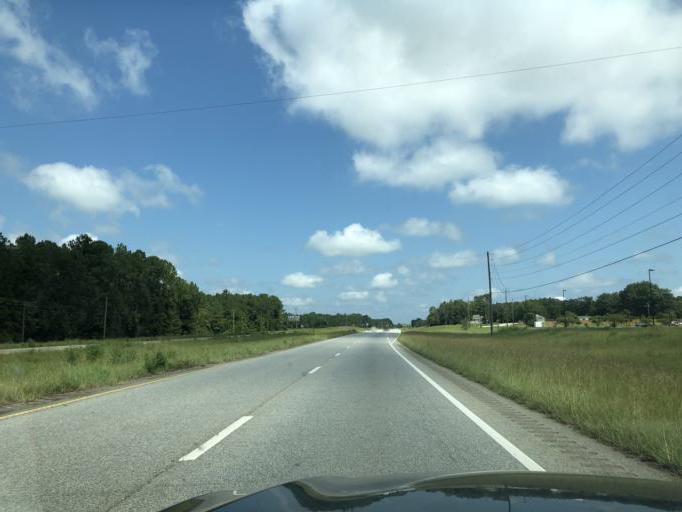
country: US
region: Alabama
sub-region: Henry County
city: Abbeville
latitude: 31.5806
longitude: -85.2801
